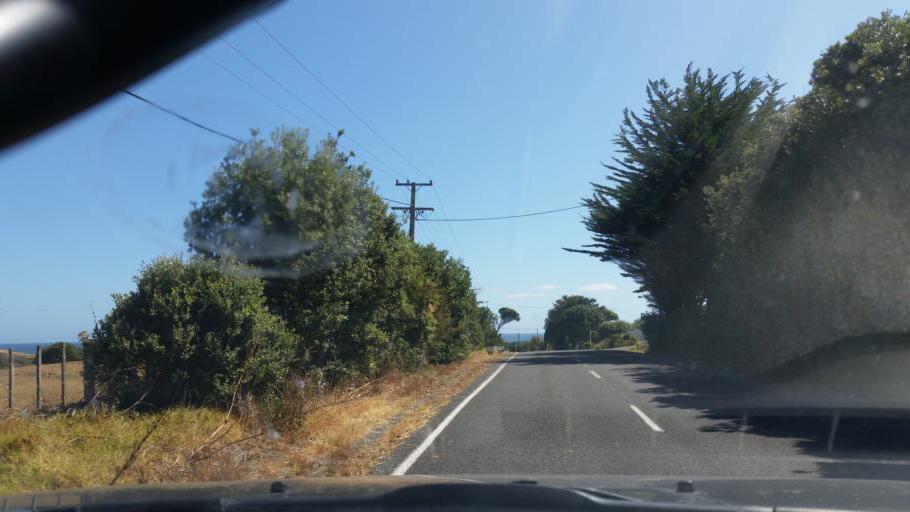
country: NZ
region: Northland
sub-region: Kaipara District
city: Dargaville
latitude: -35.9506
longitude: 173.7528
